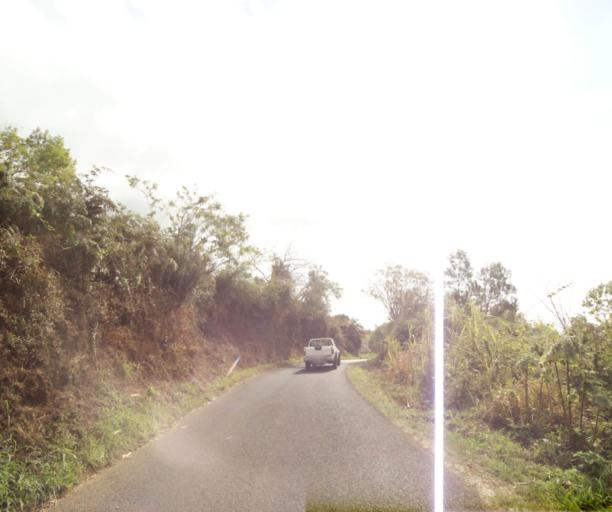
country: RE
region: Reunion
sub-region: Reunion
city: Saint-Paul
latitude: -21.0097
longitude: 55.3418
